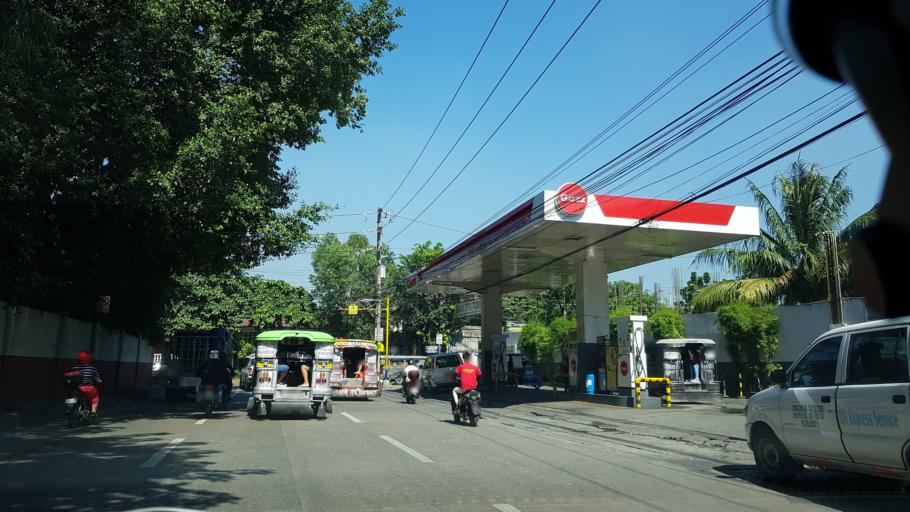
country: PH
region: Calabarzon
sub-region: Province of Rizal
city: Pateros
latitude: 14.5605
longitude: 121.0814
